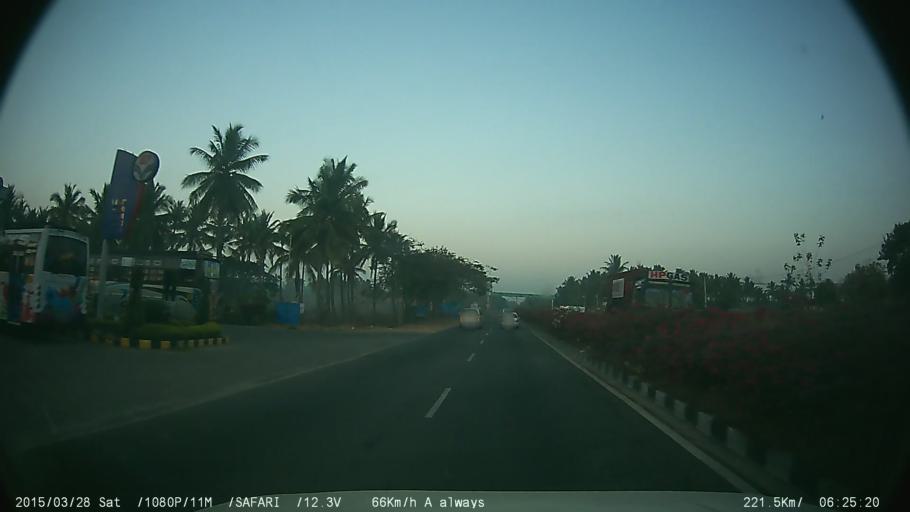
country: IN
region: Karnataka
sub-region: Ramanagara
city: Ramanagaram
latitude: 12.7080
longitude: 77.2651
